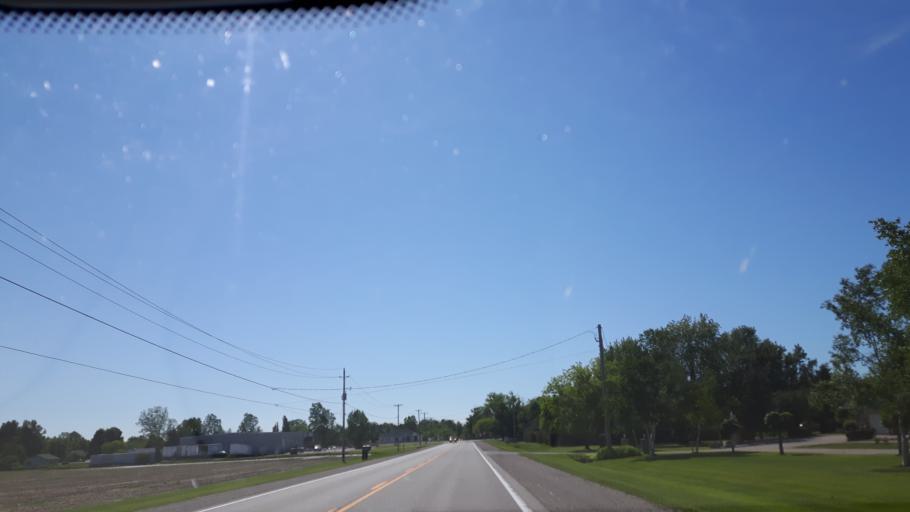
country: CA
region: Ontario
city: Bluewater
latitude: 43.4130
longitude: -81.7021
